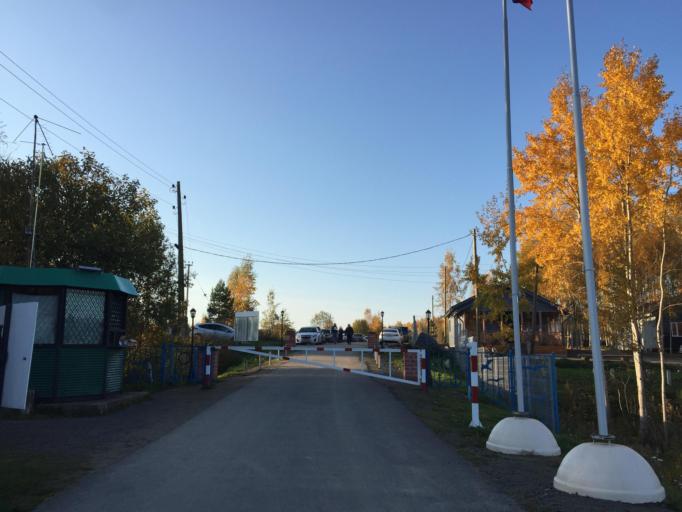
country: RU
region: Leningrad
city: Priozersk
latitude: 61.2863
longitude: 30.0895
